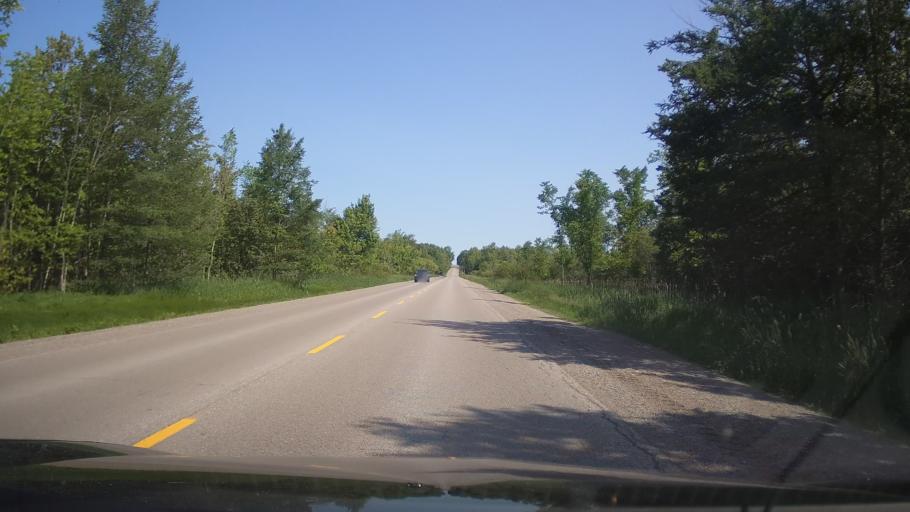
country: CA
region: Ontario
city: Uxbridge
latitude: 44.5199
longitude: -78.9601
